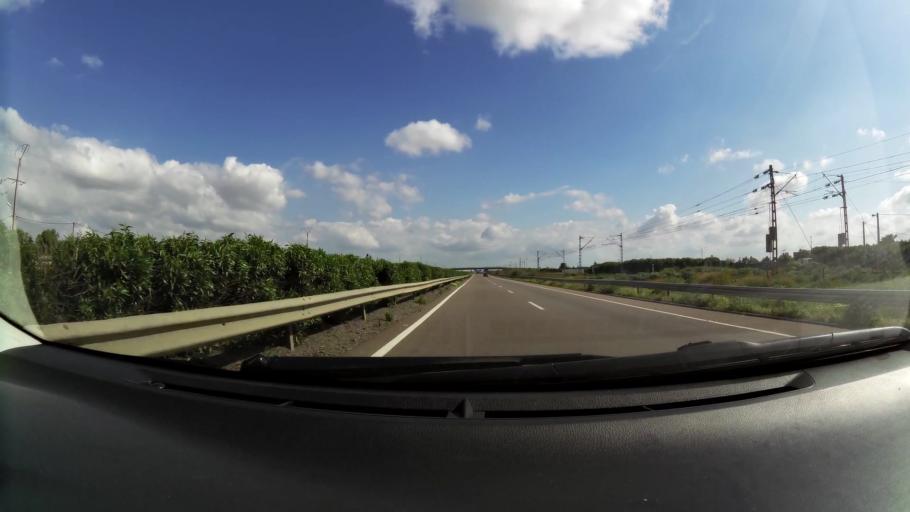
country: MA
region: Chaouia-Ouardigha
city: Nouaseur
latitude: 33.3384
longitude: -7.6115
